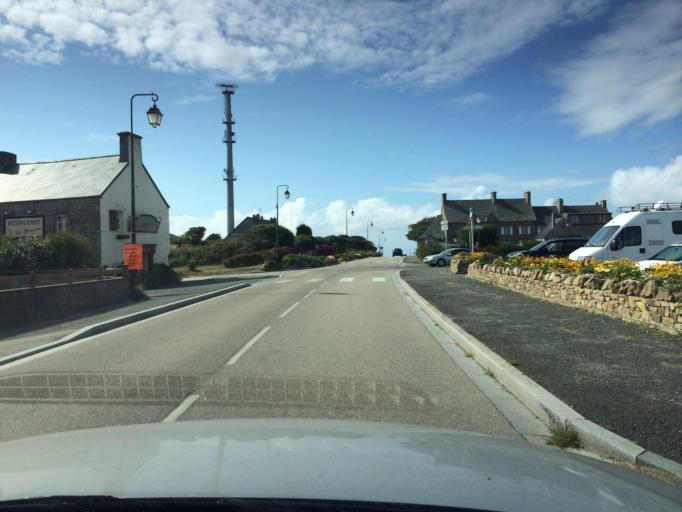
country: FR
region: Lower Normandy
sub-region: Departement de la Manche
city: Beaumont-Hague
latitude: 49.6833
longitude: -1.9047
